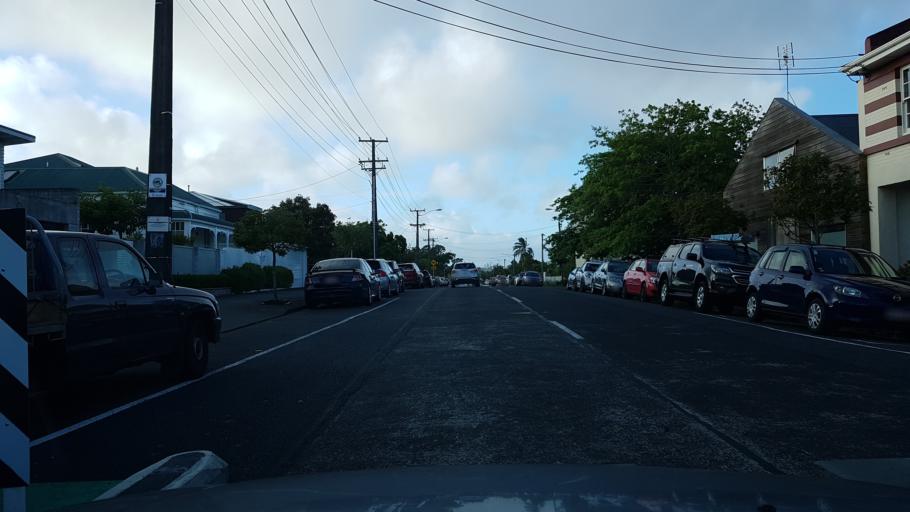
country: NZ
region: Auckland
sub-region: Auckland
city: North Shore
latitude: -36.8224
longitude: 174.7480
